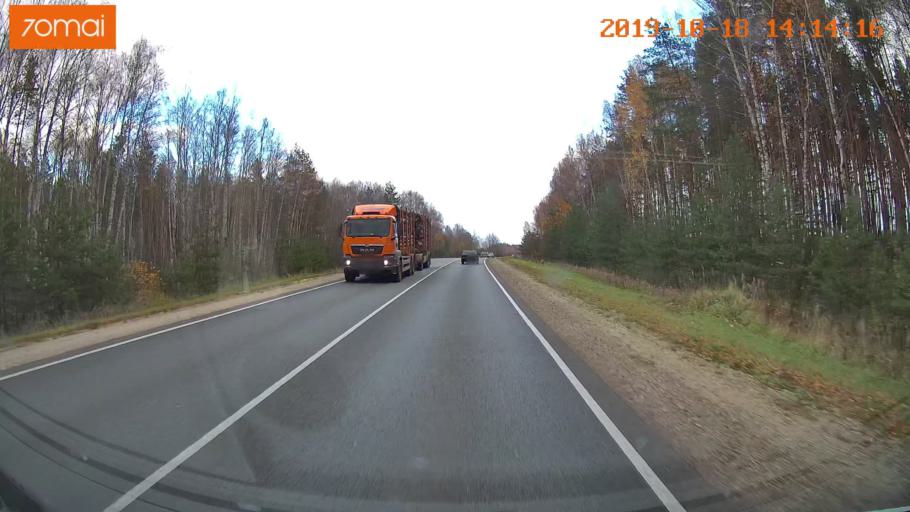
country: RU
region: Rjazan
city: Spas-Klepiki
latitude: 55.1518
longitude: 40.2912
